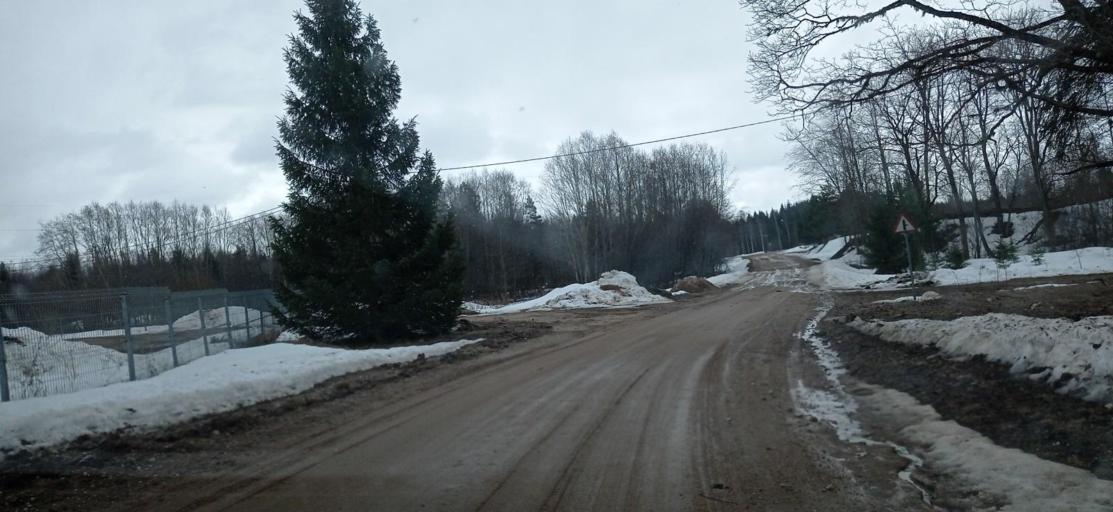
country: EE
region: Tartu
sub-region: UElenurme vald
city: Ulenurme
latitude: 58.1259
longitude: 26.6987
